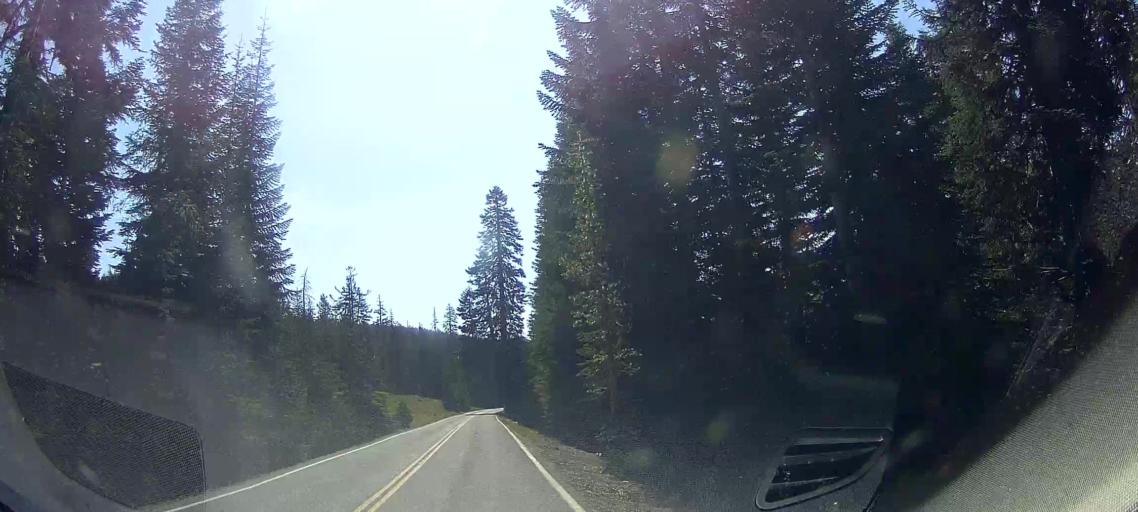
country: US
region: Oregon
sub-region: Klamath County
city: Klamath Falls
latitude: 42.8795
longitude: -122.1132
